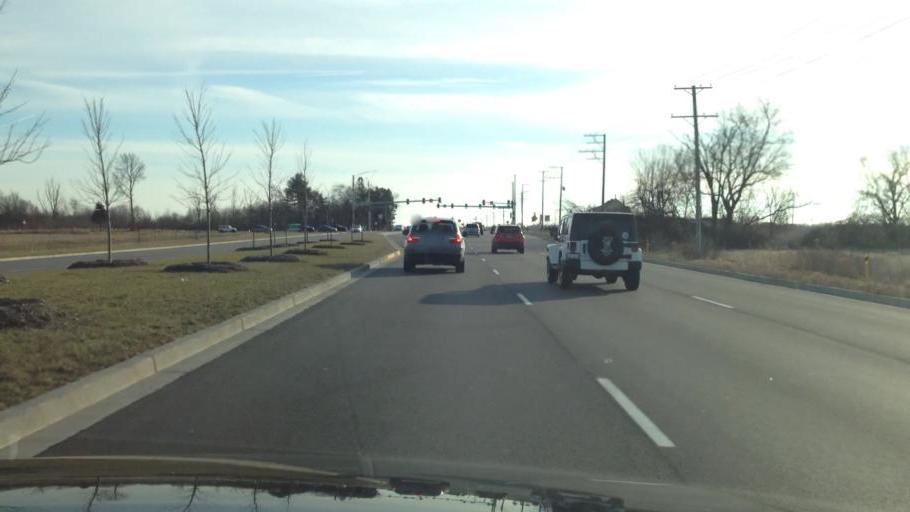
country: US
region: Illinois
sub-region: McHenry County
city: Lake in the Hills
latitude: 42.1420
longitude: -88.3358
